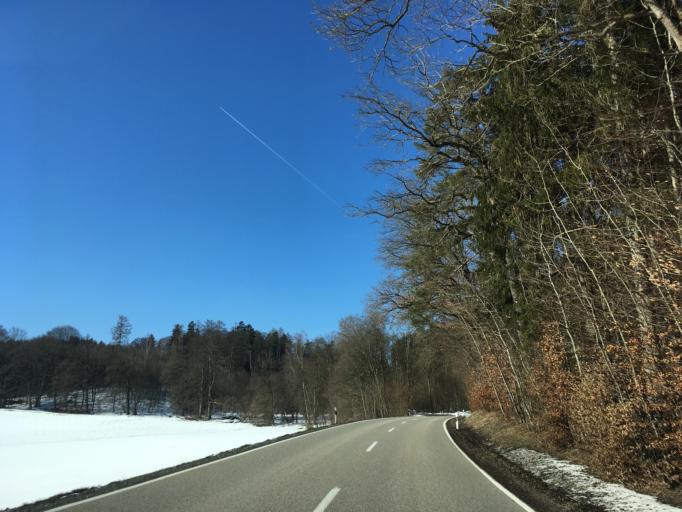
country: DE
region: Bavaria
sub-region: Upper Bavaria
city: Maitenbeth
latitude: 48.1263
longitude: 12.0859
